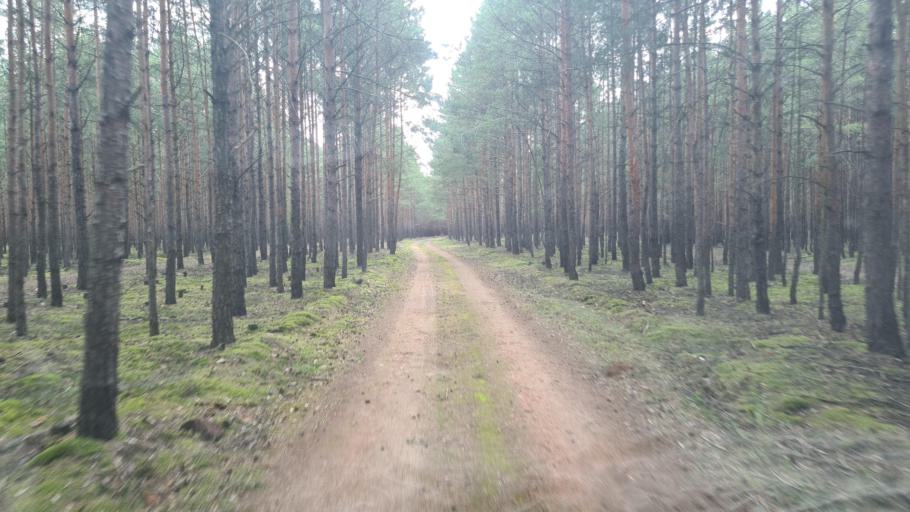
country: DE
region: Brandenburg
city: Schonewalde
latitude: 51.7518
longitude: 13.6003
